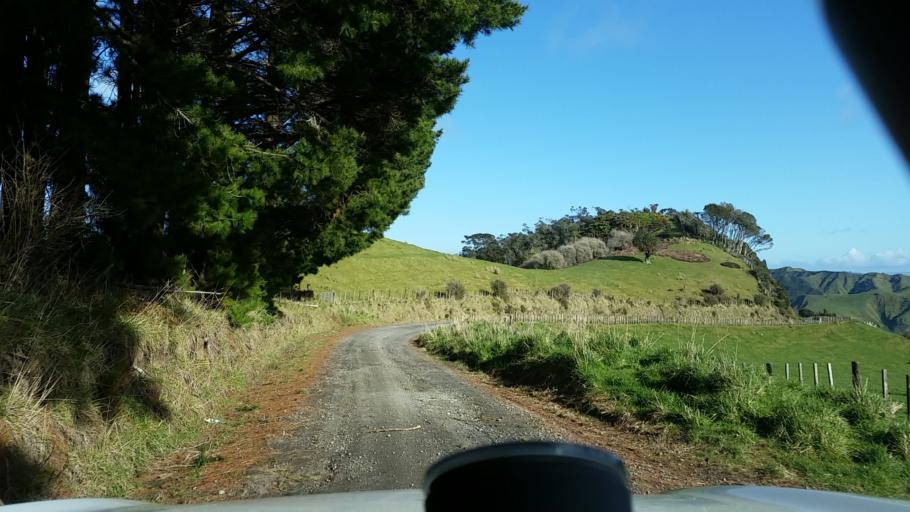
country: NZ
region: Taranaki
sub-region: South Taranaki District
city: Eltham
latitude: -39.4081
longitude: 174.5434
